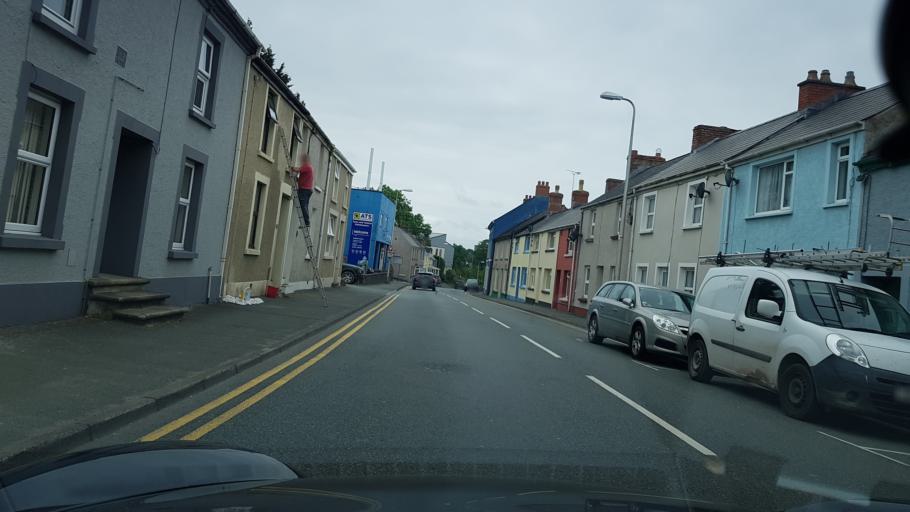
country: GB
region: Wales
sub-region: Pembrokeshire
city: Haverfordwest
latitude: 51.8079
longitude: -4.9647
